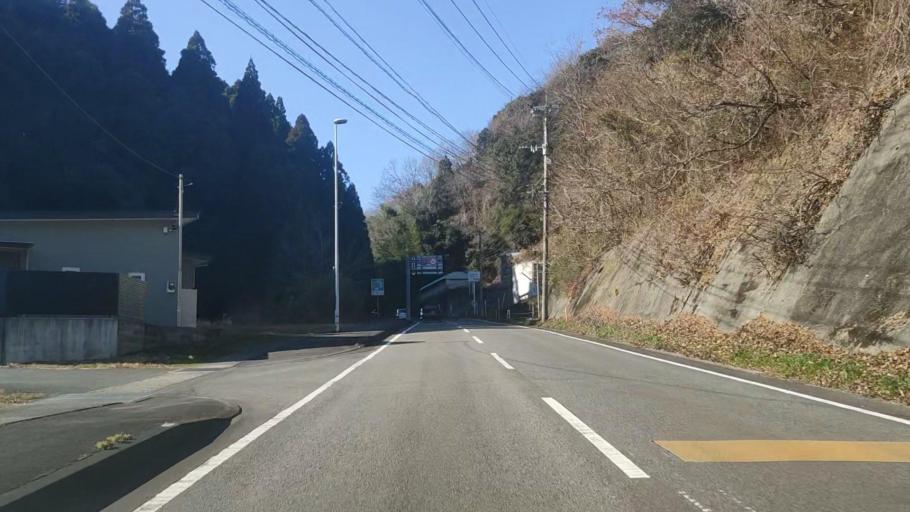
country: JP
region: Oita
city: Saiki
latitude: 32.9746
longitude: 131.8622
